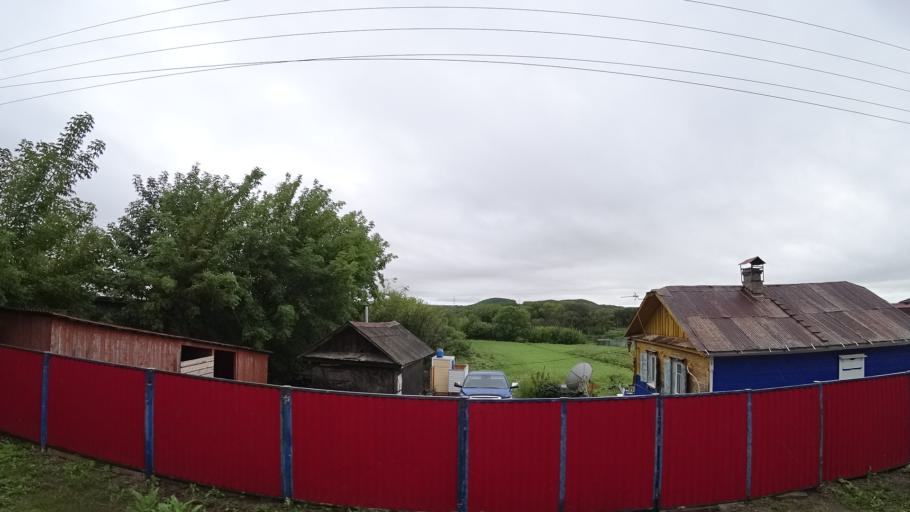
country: RU
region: Primorskiy
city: Monastyrishche
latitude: 44.2640
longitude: 132.4045
